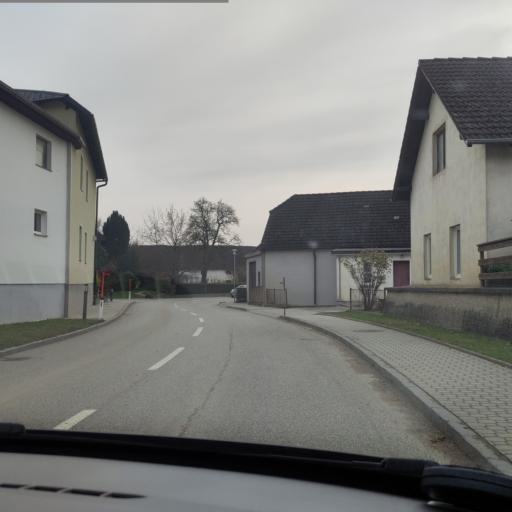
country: AT
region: Lower Austria
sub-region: Politischer Bezirk Sankt Polten
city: Karlstetten
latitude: 48.2402
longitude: 15.5630
